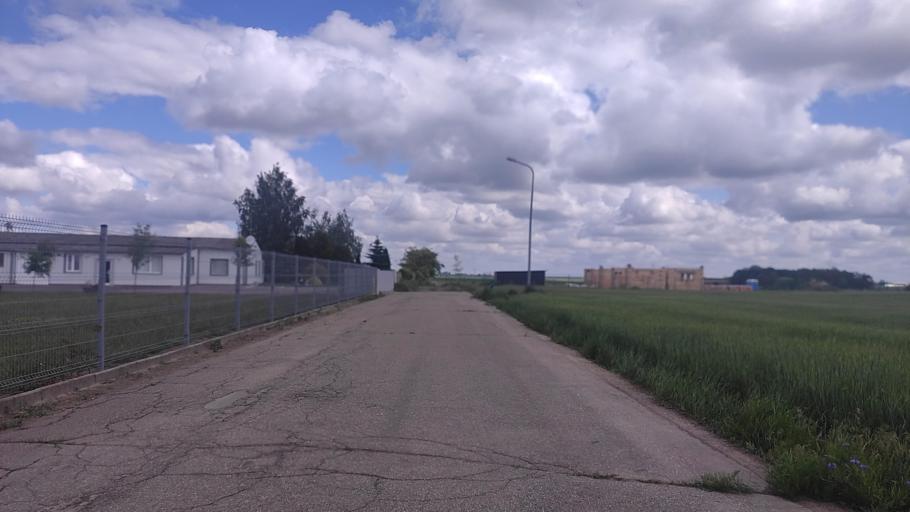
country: PL
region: Greater Poland Voivodeship
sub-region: Powiat poznanski
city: Kostrzyn
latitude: 52.4171
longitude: 17.1709
